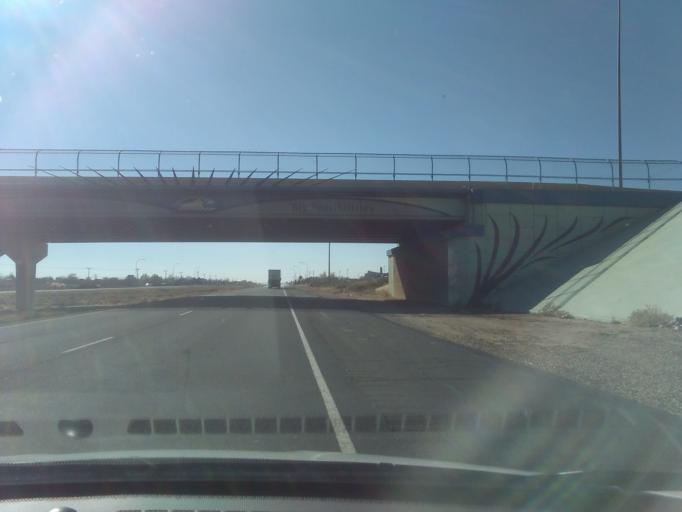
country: US
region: New Mexico
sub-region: Valencia County
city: Los Lunas
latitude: 34.8149
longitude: -106.7612
